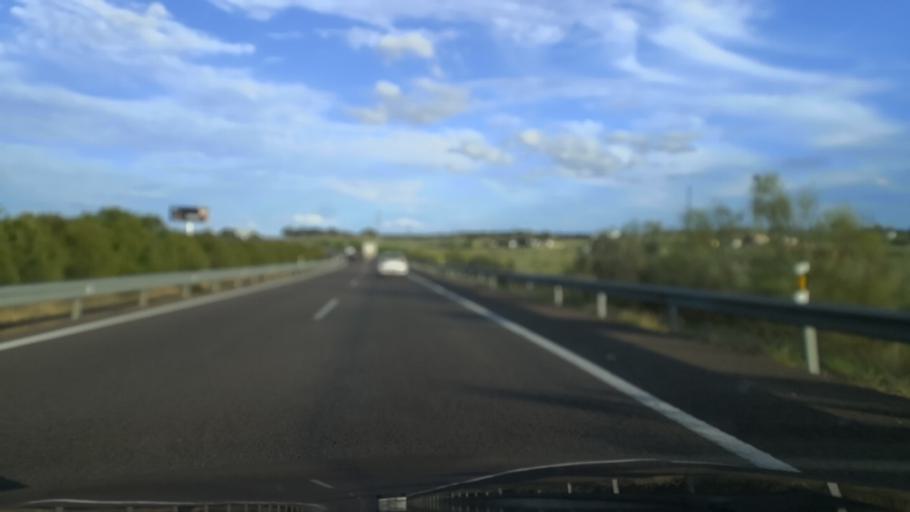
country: ES
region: Extremadura
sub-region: Provincia de Badajoz
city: Badajoz
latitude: 38.8804
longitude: -6.8872
